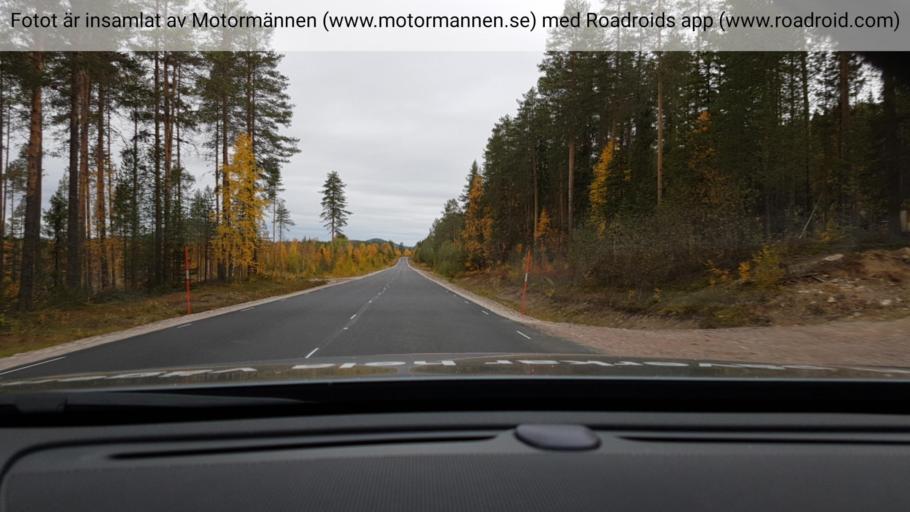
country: SE
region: Norrbotten
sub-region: Overkalix Kommun
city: OEverkalix
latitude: 66.3960
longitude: 22.8164
